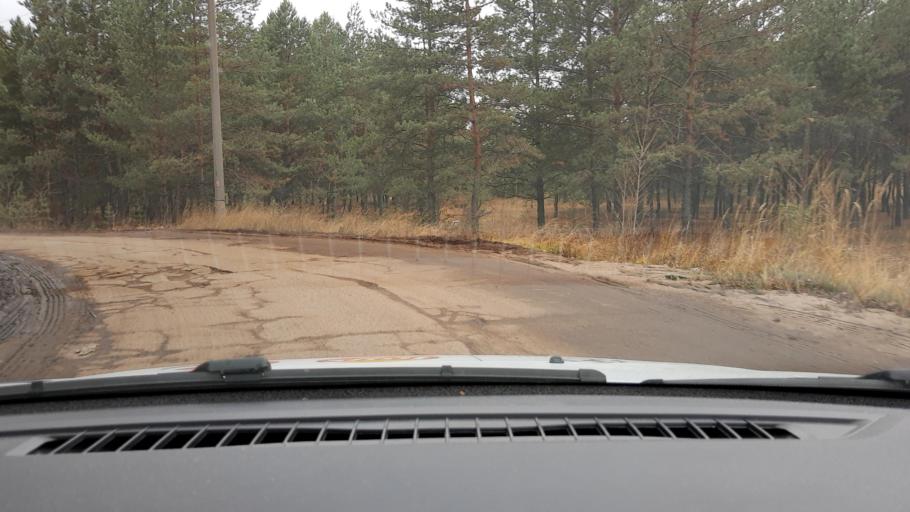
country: RU
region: Nizjnij Novgorod
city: Dzerzhinsk
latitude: 56.2783
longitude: 43.4778
